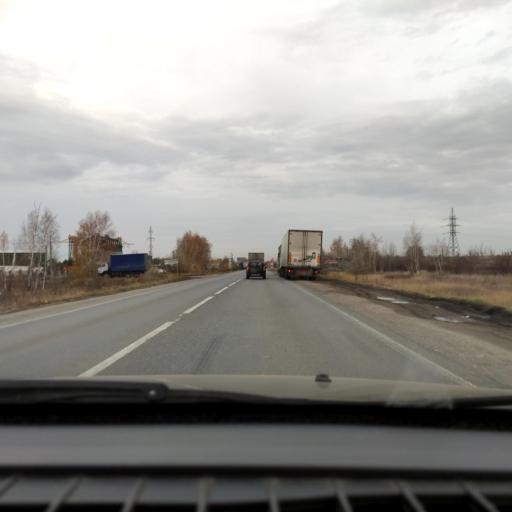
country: RU
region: Samara
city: Tol'yatti
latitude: 53.5628
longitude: 49.3548
